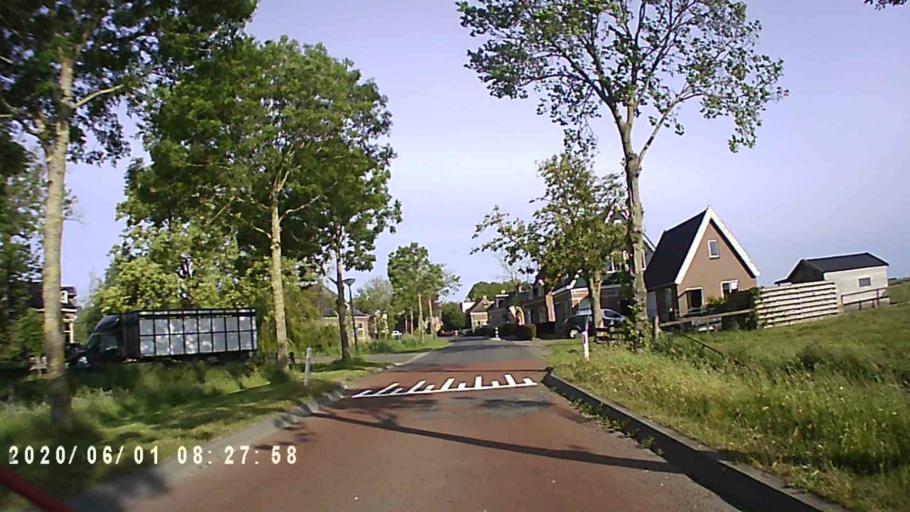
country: NL
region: Friesland
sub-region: Gemeente Ferwerderadiel
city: Burdaard
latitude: 53.3009
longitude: 5.8525
